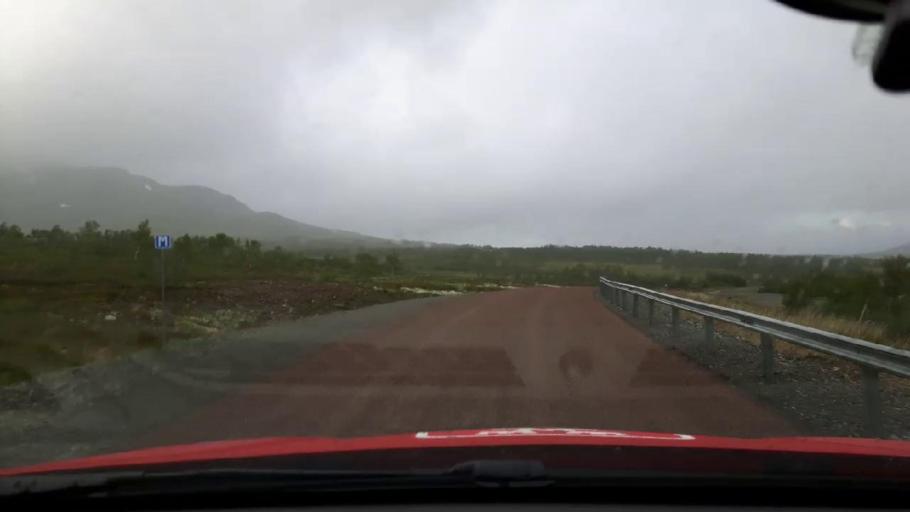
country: NO
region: Nord-Trondelag
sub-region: Meraker
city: Meraker
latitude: 63.1989
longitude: 12.3893
